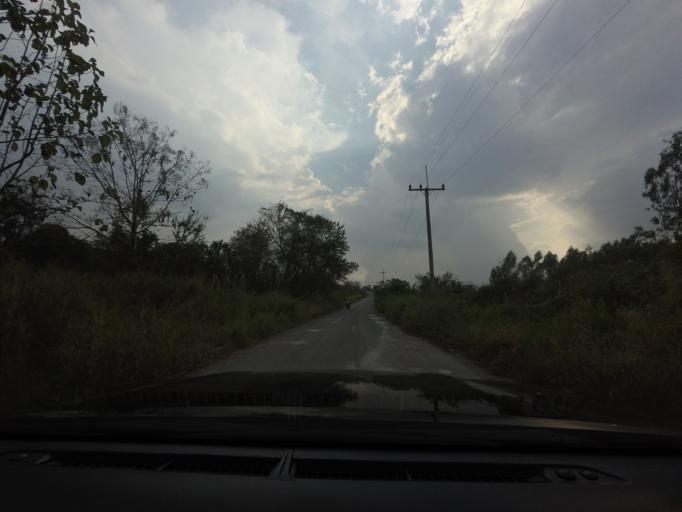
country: TH
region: Nakhon Ratchasima
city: Wang Nam Khiao
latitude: 14.4138
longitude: 101.7952
